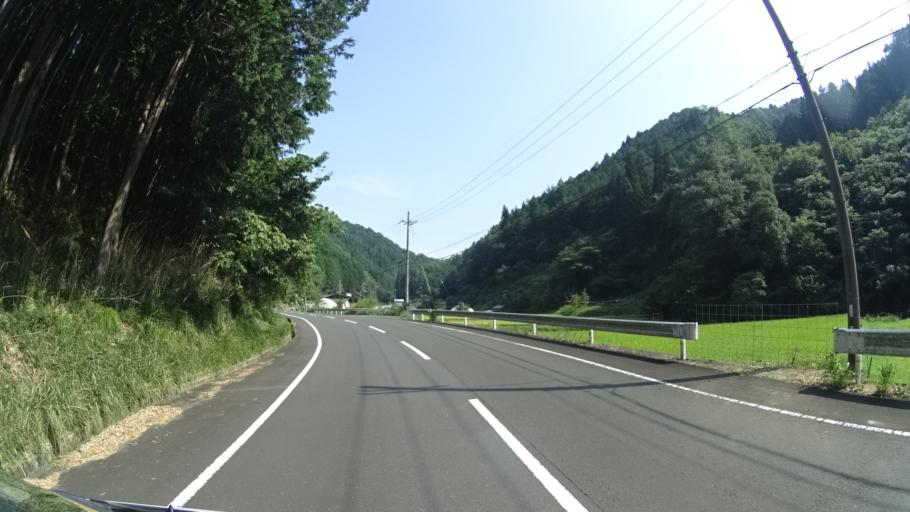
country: JP
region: Kyoto
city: Maizuru
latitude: 35.4179
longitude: 135.2269
